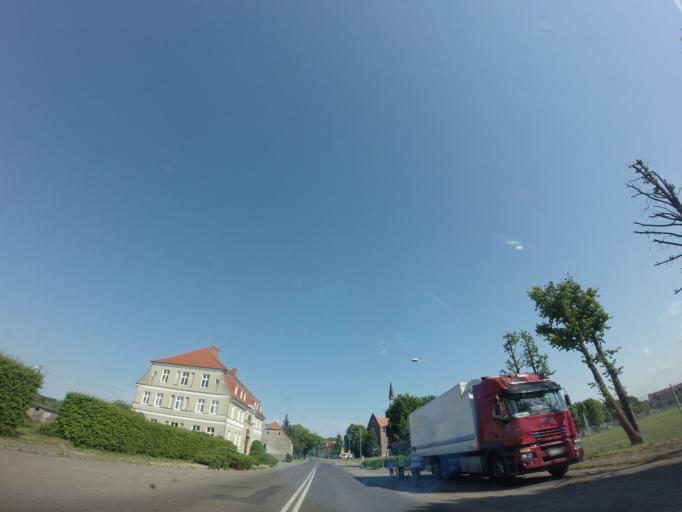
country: PL
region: West Pomeranian Voivodeship
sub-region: Powiat gryfinski
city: Stare Czarnowo
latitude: 53.3025
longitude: 14.8115
